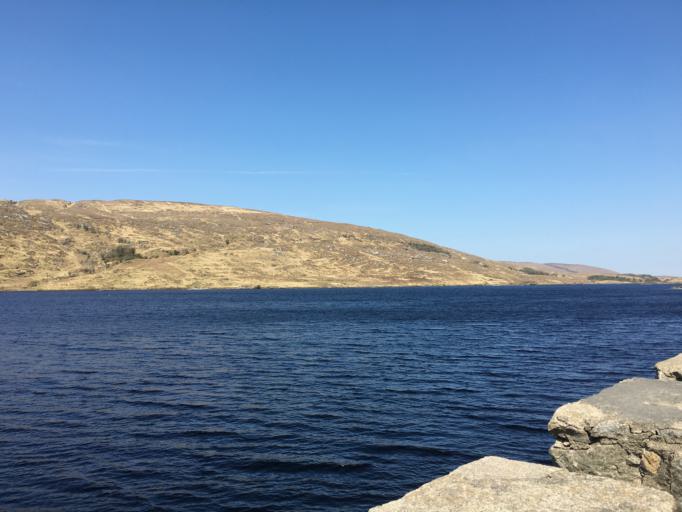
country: IE
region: Ulster
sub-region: County Donegal
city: Dunlewy
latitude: 55.0367
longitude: -7.9690
